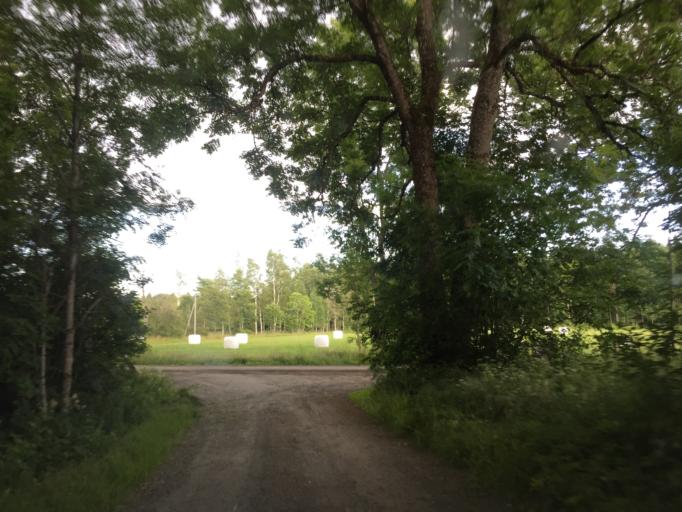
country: SE
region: OEstergoetland
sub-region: Motala Kommun
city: Ryd
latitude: 58.7061
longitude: 15.0508
